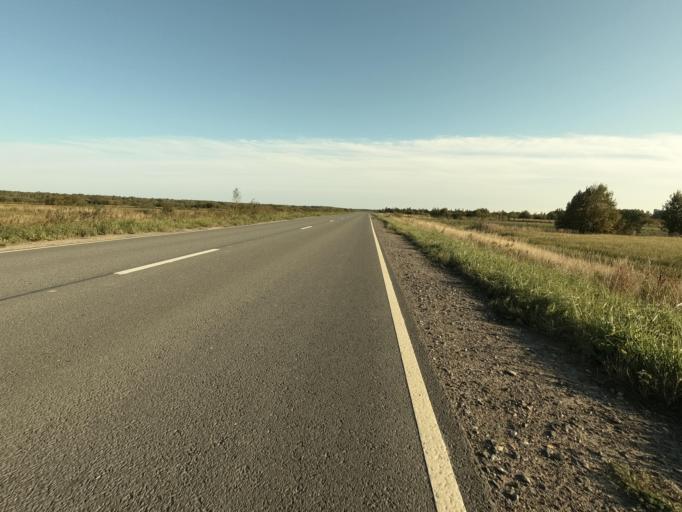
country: RU
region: St.-Petersburg
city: Sapernyy
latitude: 59.7500
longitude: 30.6388
